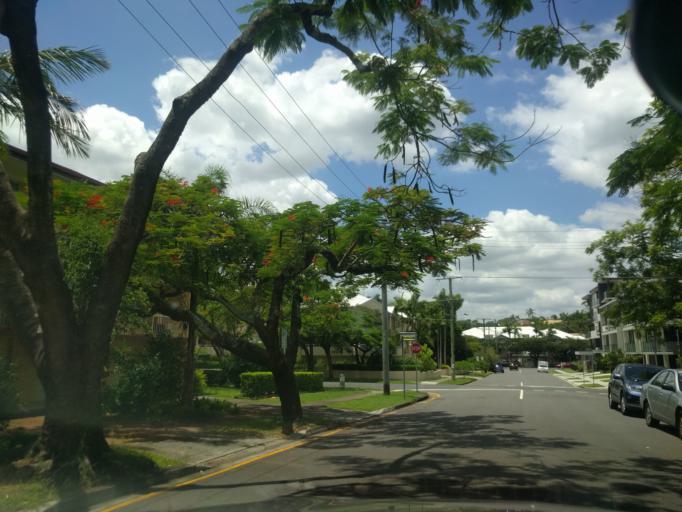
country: AU
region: Queensland
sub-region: Brisbane
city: Toowong
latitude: -27.4930
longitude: 153.0031
